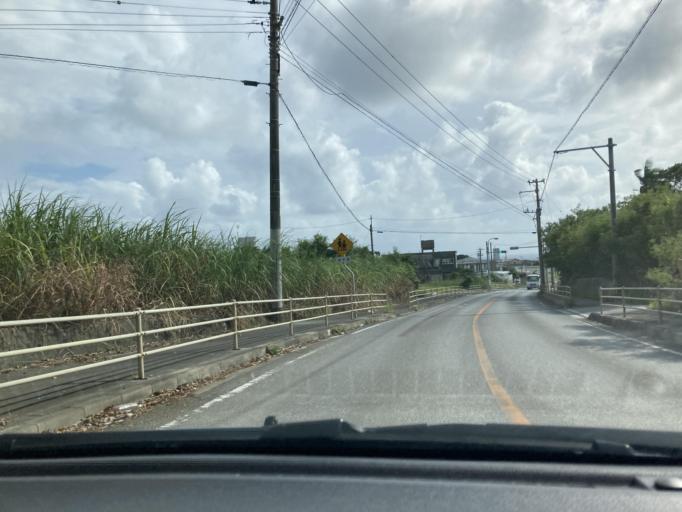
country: JP
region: Okinawa
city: Itoman
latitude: 26.0978
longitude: 127.6995
